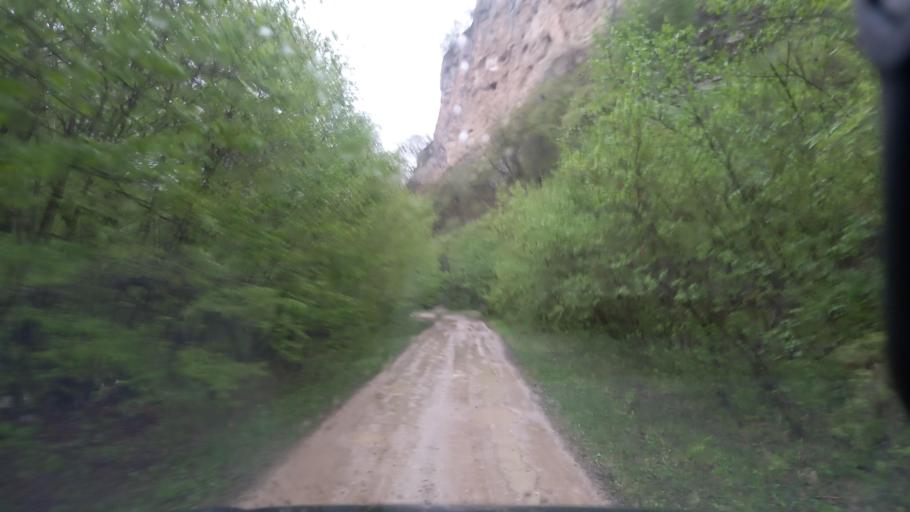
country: RU
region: Kabardino-Balkariya
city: Bylym
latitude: 43.5885
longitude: 43.0218
